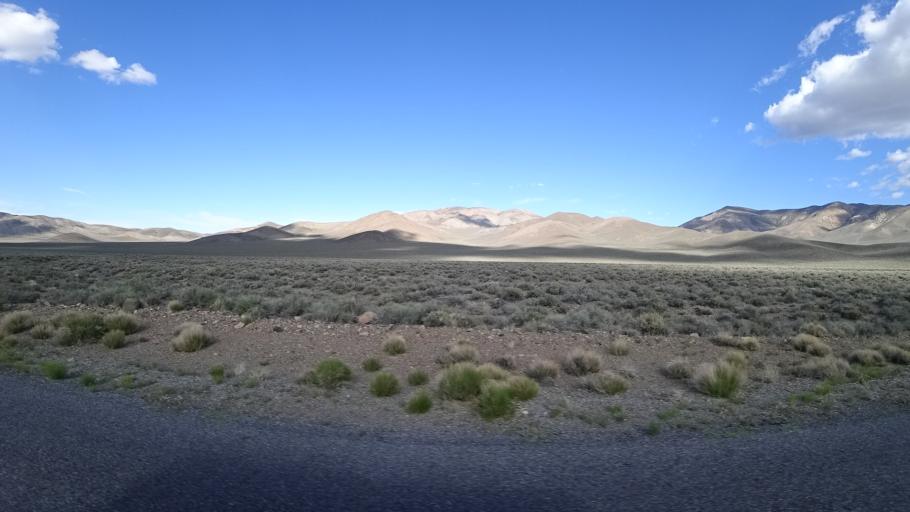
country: US
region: California
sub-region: San Bernardino County
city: Searles Valley
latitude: 36.3429
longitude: -117.1354
